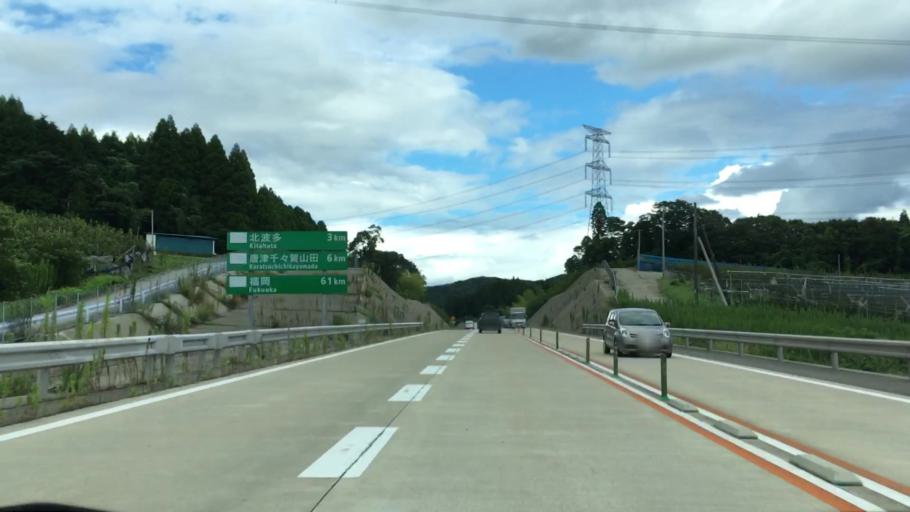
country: JP
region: Saga Prefecture
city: Imaricho-ko
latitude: 33.3540
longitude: 129.9258
